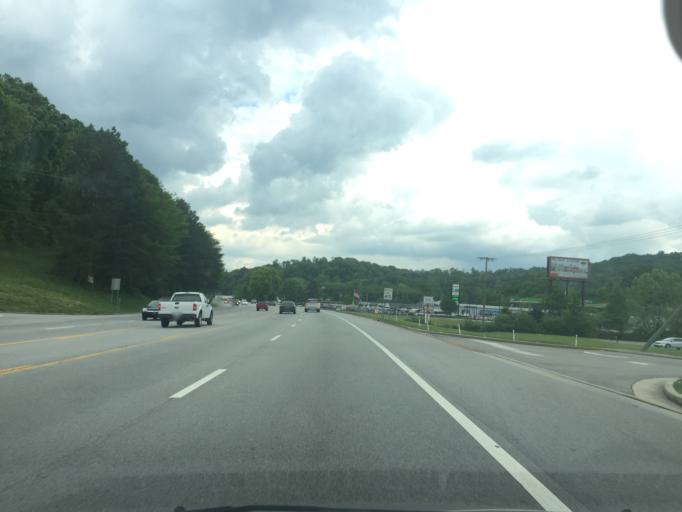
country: US
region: Tennessee
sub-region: Hamilton County
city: Harrison
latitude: 35.1190
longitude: -85.1254
